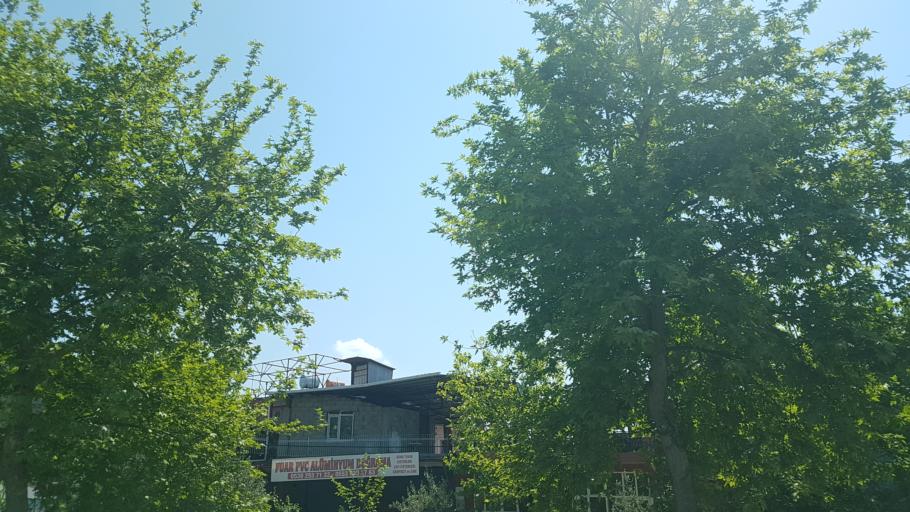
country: TR
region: Adana
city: Yuregir
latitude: 37.0150
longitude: 35.3848
